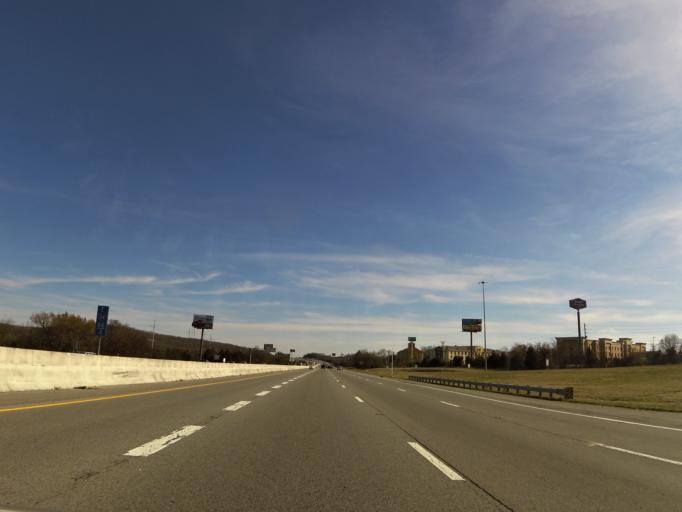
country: US
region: Tennessee
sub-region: Rutherford County
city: La Vergne
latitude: 35.9741
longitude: -86.5709
